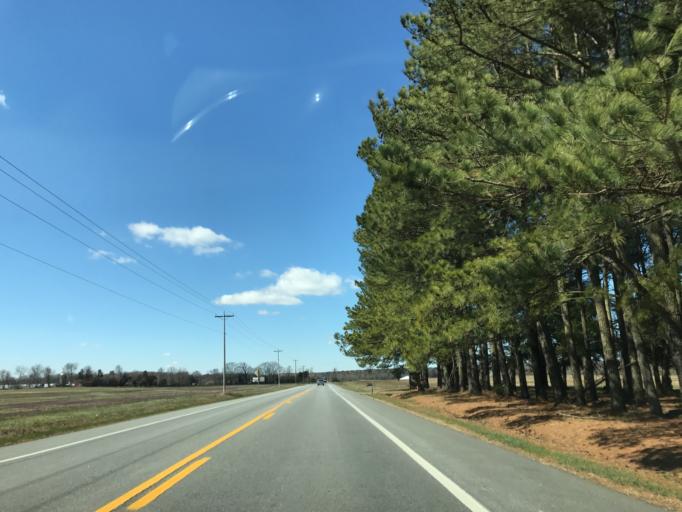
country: US
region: Maryland
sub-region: Caroline County
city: Ridgely
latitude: 39.1076
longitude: -75.8995
